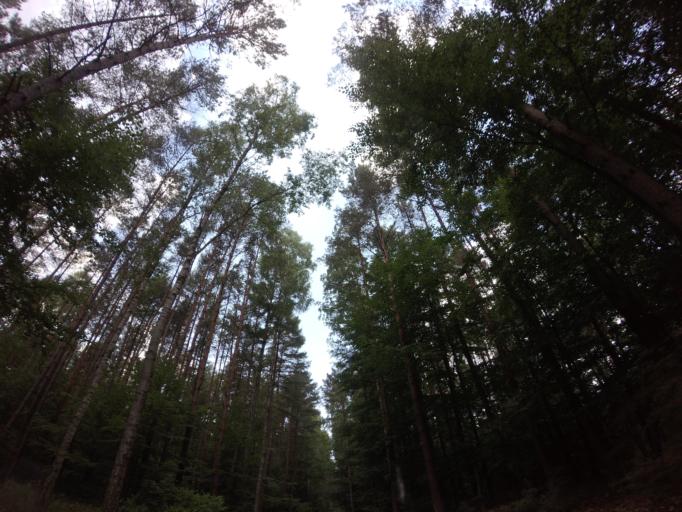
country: PL
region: West Pomeranian Voivodeship
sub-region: Powiat choszczenski
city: Bierzwnik
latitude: 53.0819
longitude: 15.6729
